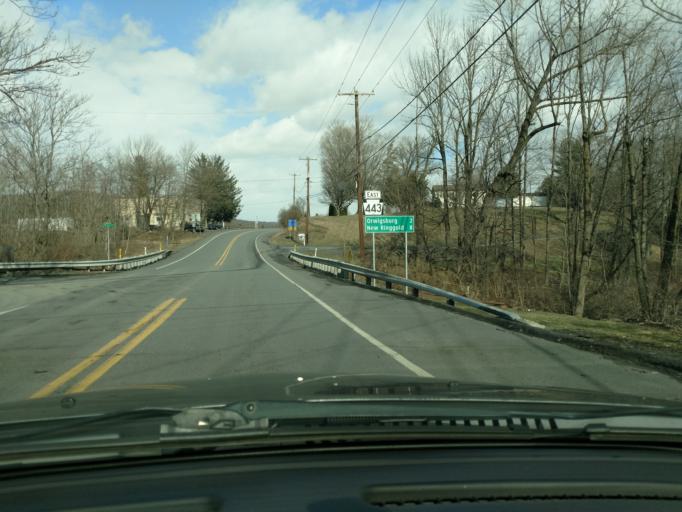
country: US
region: Pennsylvania
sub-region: Schuylkill County
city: Schuylkill Haven
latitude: 40.6464
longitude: -76.1382
